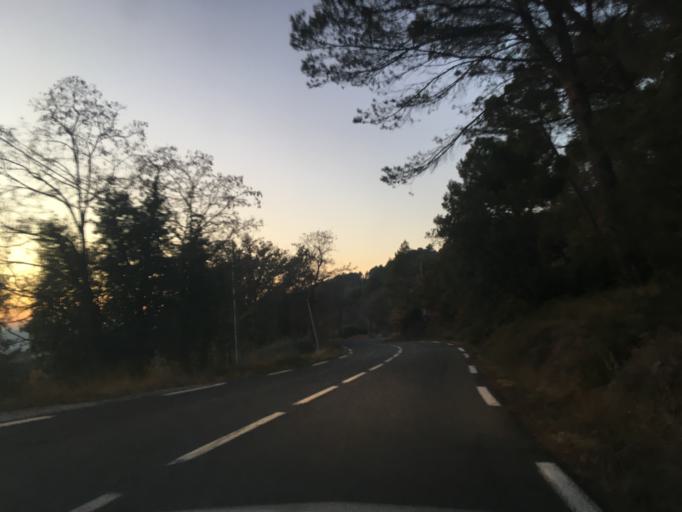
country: FR
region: Provence-Alpes-Cote d'Azur
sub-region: Departement du Var
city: Draguignan
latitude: 43.5347
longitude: 6.4986
